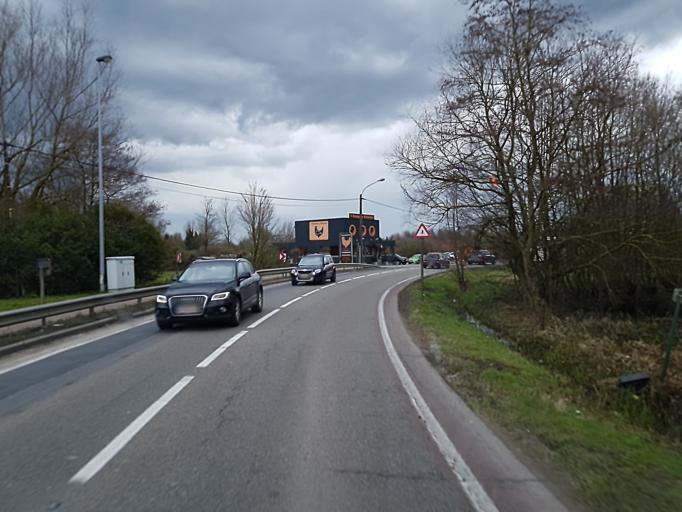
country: BE
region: Flanders
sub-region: Provincie Antwerpen
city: Nijlen
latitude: 51.1799
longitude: 4.6322
